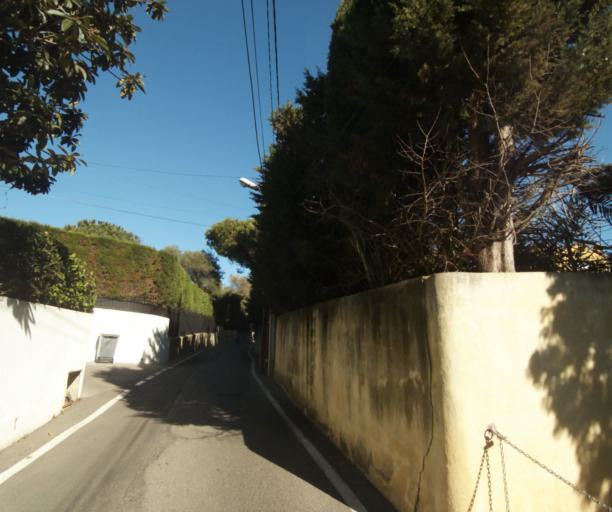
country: FR
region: Provence-Alpes-Cote d'Azur
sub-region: Departement des Alpes-Maritimes
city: Antibes
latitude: 43.5607
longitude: 7.1276
